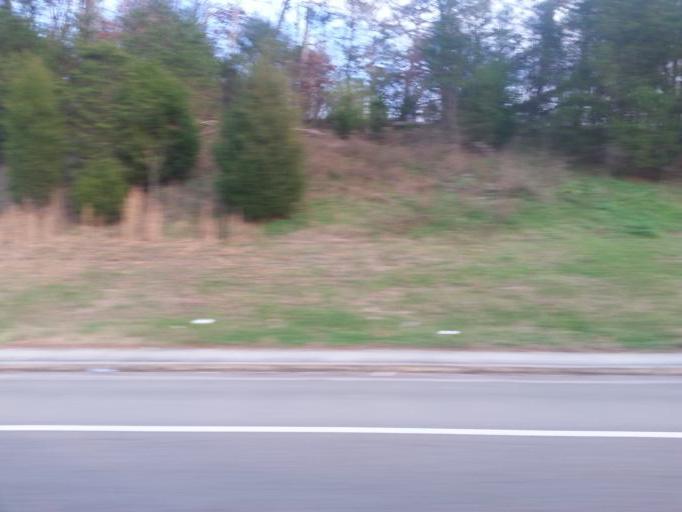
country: US
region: Tennessee
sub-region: Rhea County
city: Dayton
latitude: 35.5187
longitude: -84.9981
